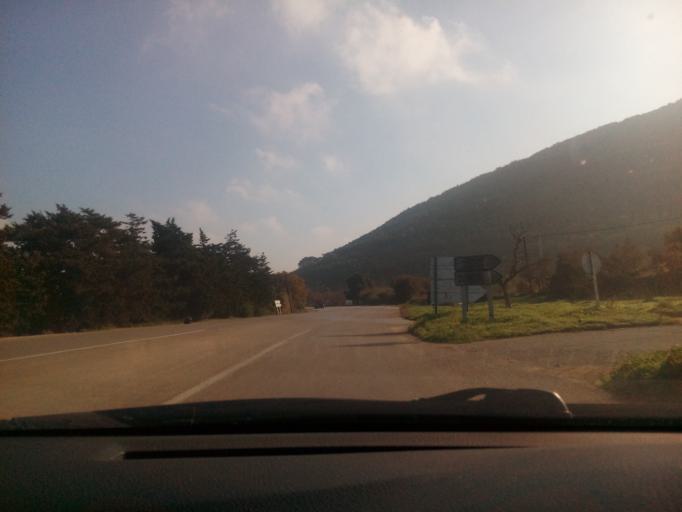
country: DZ
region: Oran
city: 'Ain el Turk
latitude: 35.7041
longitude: -0.8385
